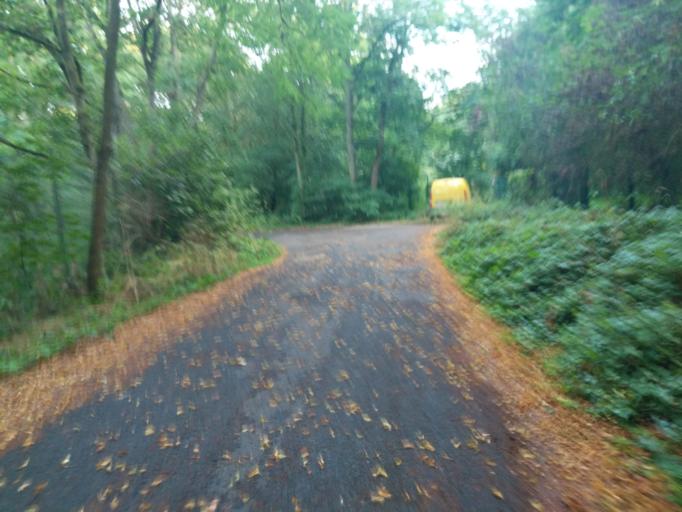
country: DE
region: North Rhine-Westphalia
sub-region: Regierungsbezirk Dusseldorf
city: Meerbusch
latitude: 51.3314
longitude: 6.6611
